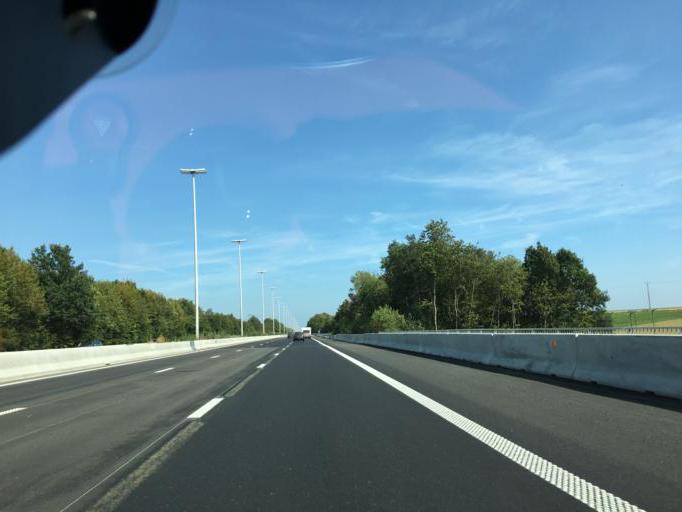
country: BE
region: Wallonia
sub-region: Province de Liege
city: Heron
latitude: 50.5306
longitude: 5.0568
